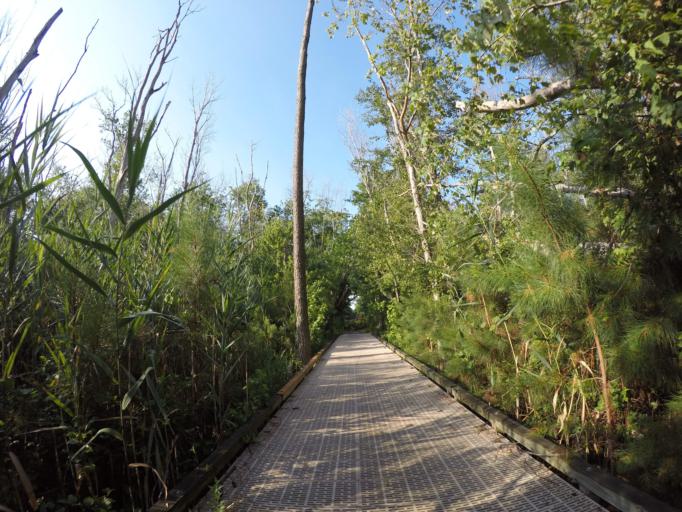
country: US
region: Delaware
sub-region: Sussex County
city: Ocean View
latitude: 38.5562
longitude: -75.0704
